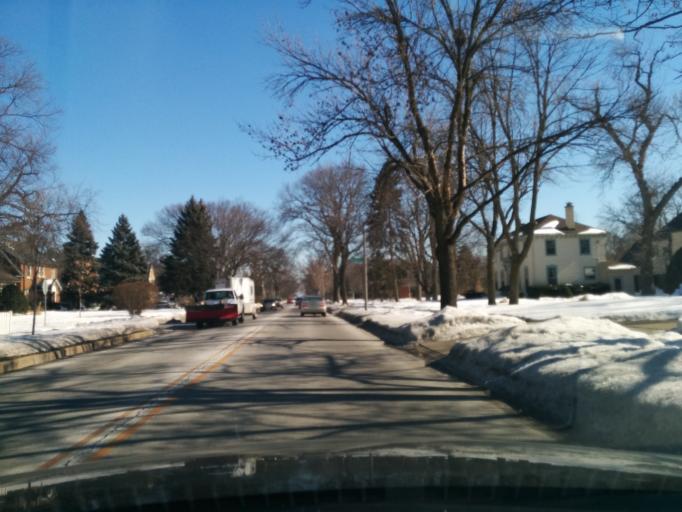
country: US
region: Illinois
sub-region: DuPage County
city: Elmhurst
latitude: 41.8902
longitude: -87.9356
